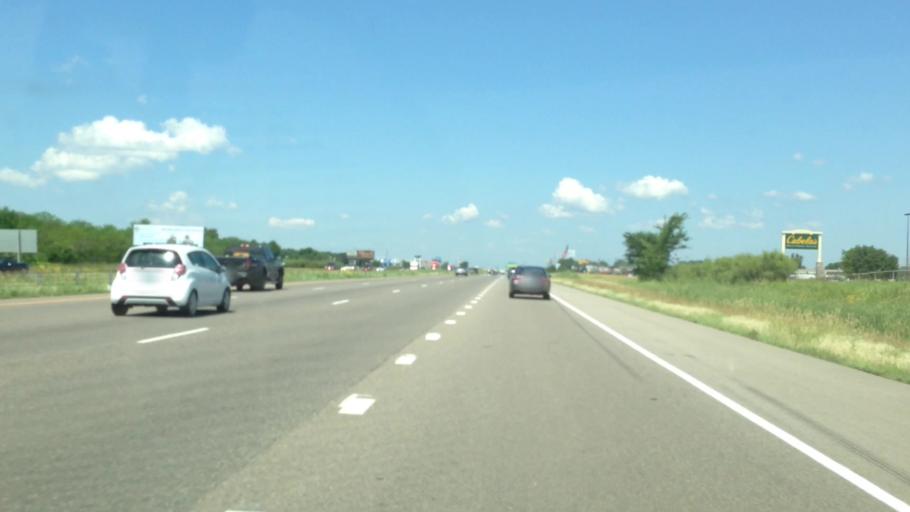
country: US
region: Minnesota
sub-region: Hennepin County
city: Rogers
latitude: 45.1854
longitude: -93.5387
